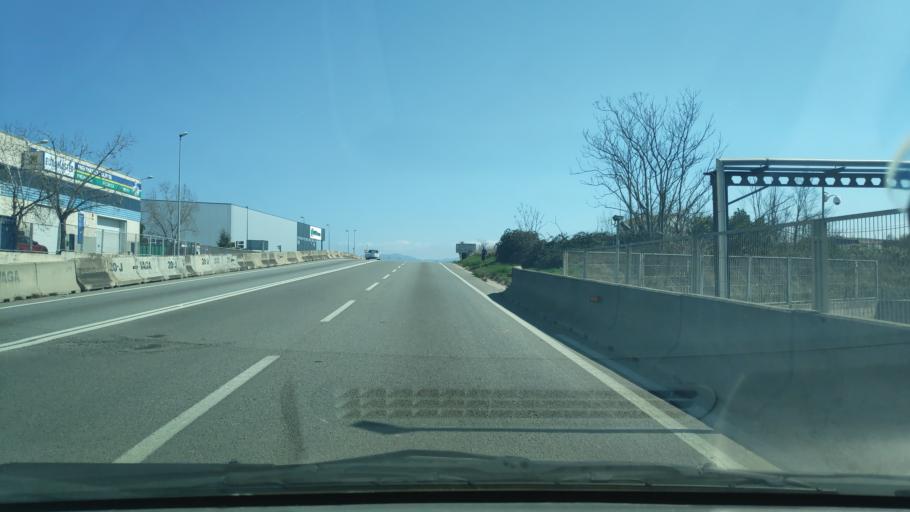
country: ES
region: Catalonia
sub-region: Provincia de Barcelona
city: Polinya
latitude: 41.5337
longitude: 2.1598
